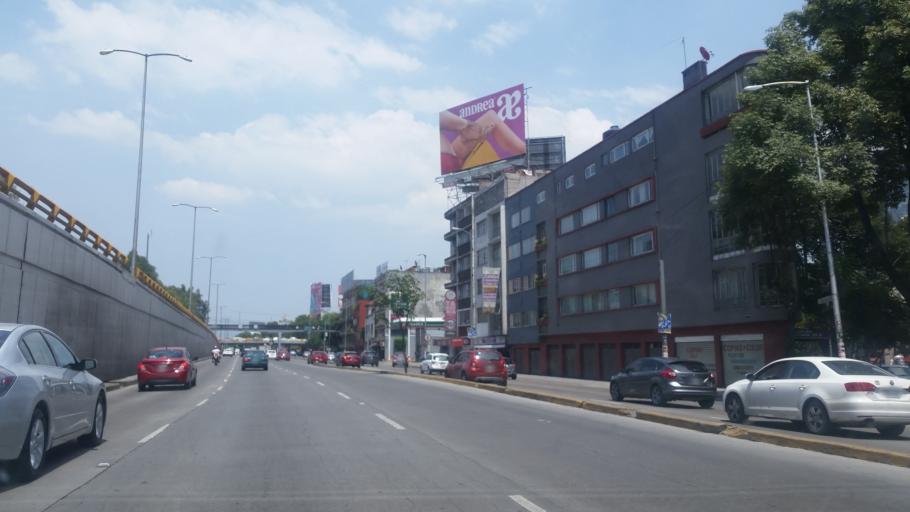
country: MX
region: Mexico City
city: Miguel Hidalgo
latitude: 19.4271
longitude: -99.1754
